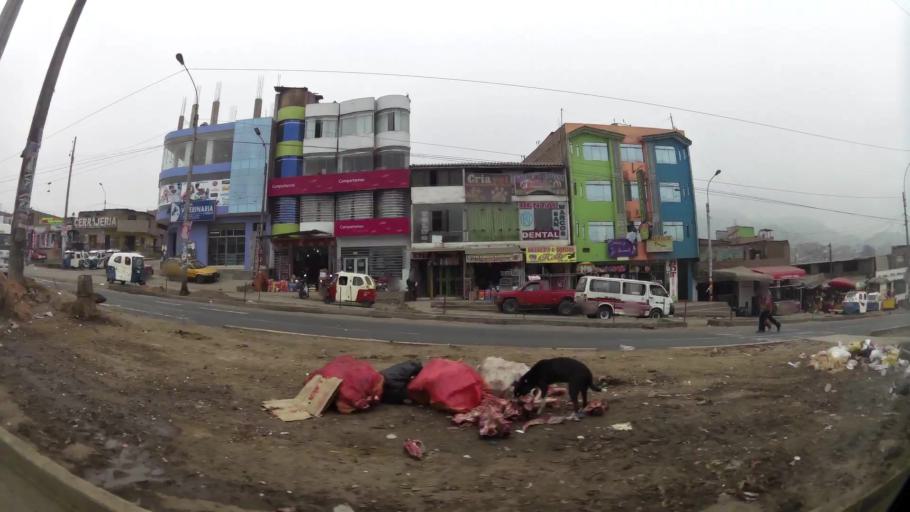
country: PE
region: Lima
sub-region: Lima
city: Urb. Santo Domingo
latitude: -11.8783
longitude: -77.0184
